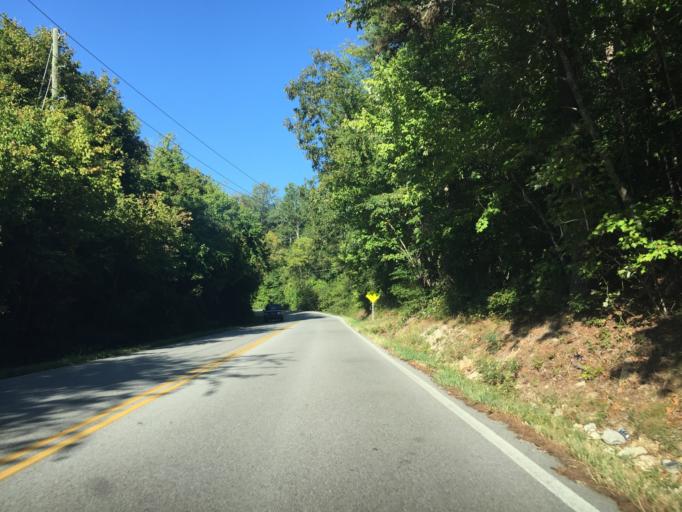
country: US
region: Tennessee
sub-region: Hamilton County
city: Harrison
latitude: 35.1188
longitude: -85.1155
